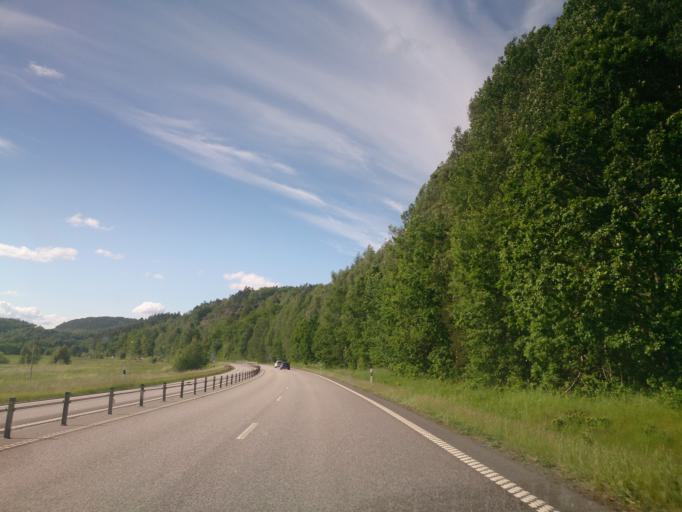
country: SE
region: OEstergoetland
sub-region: Norrkopings Kommun
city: Jursla
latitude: 58.6671
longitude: 16.1661
